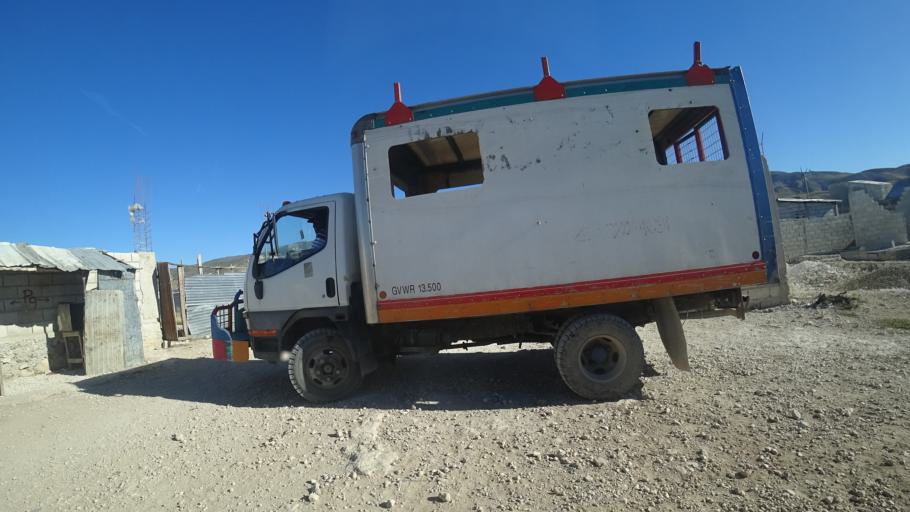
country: HT
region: Ouest
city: Cabaret
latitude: 18.6868
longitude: -72.3222
